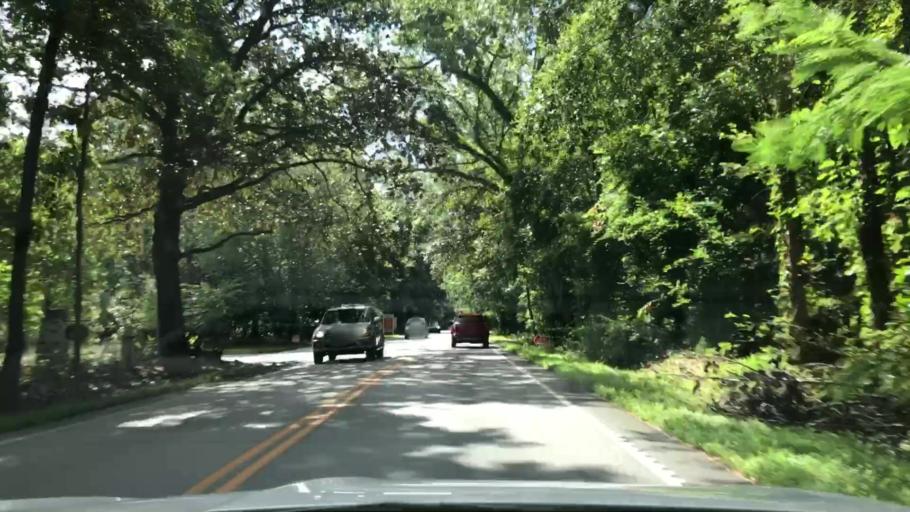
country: US
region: South Carolina
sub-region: Charleston County
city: Shell Point
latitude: 32.8531
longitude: -80.0694
